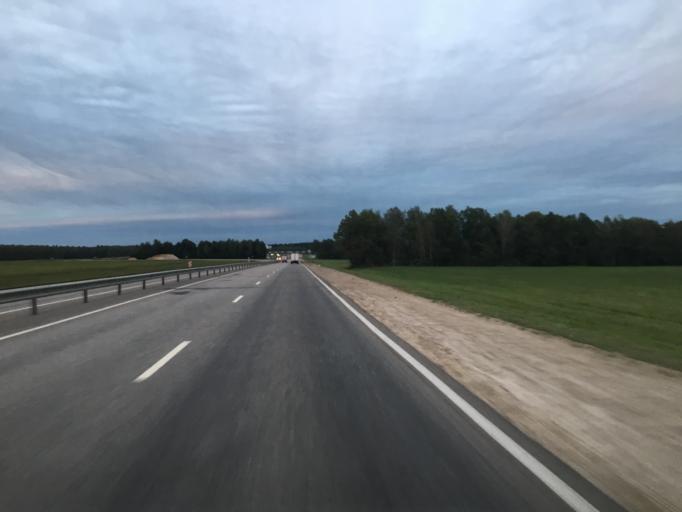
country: RU
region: Kaluga
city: Detchino
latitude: 54.6711
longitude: 36.2891
